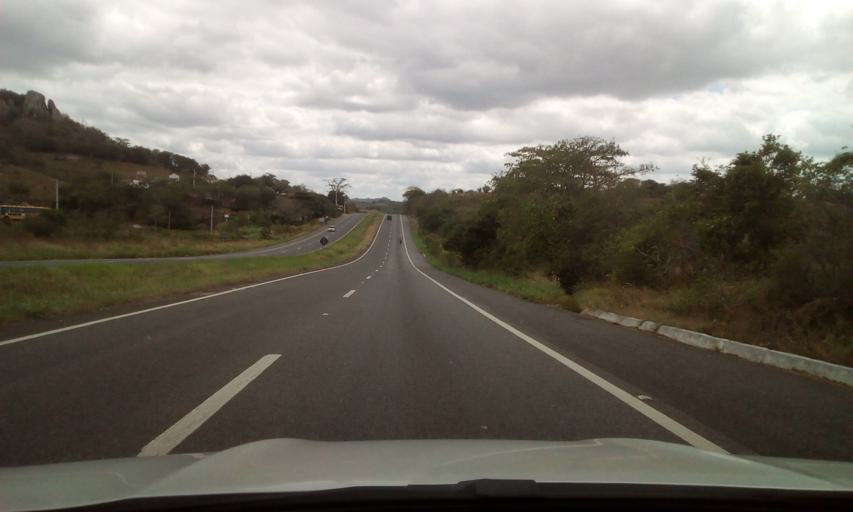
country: BR
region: Paraiba
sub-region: Fagundes
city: Fagundes
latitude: -7.2732
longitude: -35.7250
